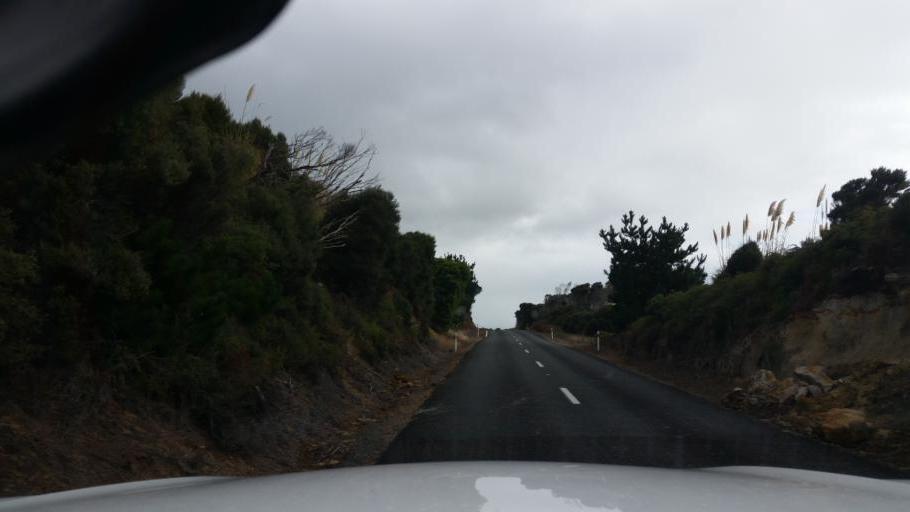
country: NZ
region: Northland
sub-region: Kaipara District
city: Dargaville
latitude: -35.8289
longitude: 173.6543
